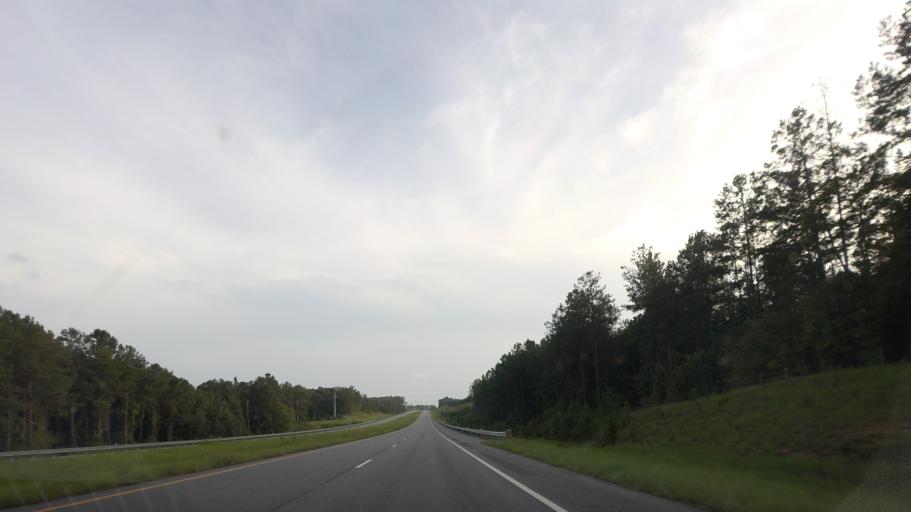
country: US
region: Georgia
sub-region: Wilkinson County
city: Gordon
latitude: 32.8707
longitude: -83.3762
